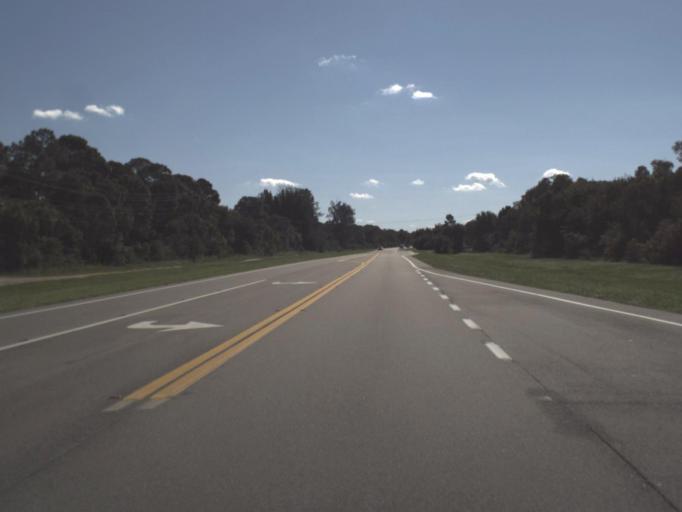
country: US
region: Florida
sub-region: Lee County
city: Lehigh Acres
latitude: 26.5550
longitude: -81.6522
